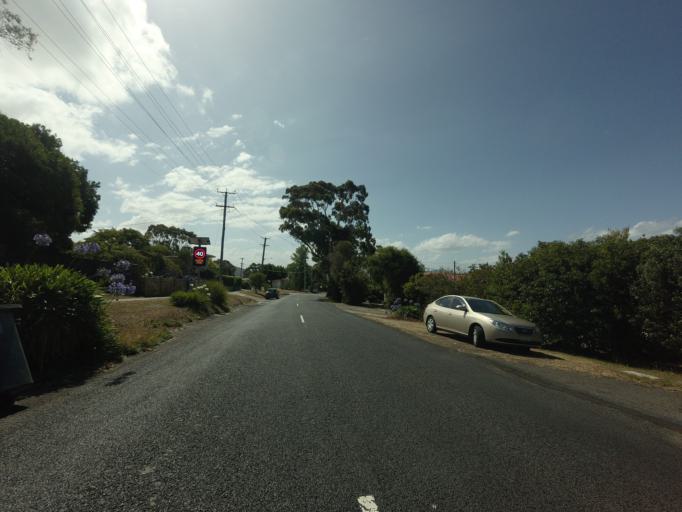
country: AU
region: Tasmania
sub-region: Hobart
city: Dynnyrne
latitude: -42.9149
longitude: 147.3239
